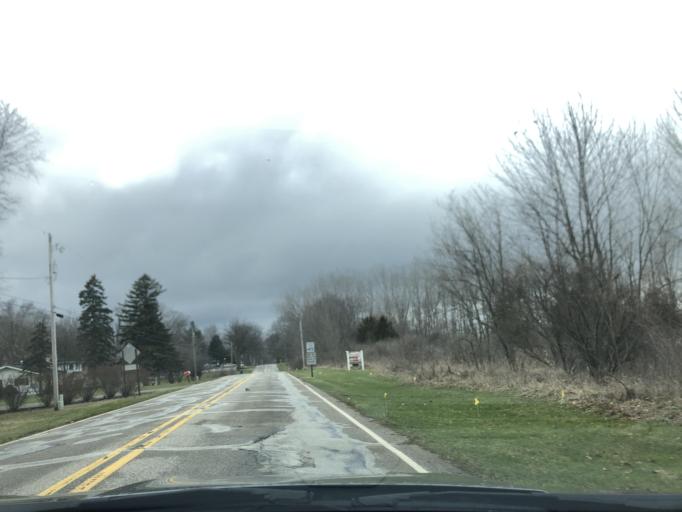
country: US
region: Michigan
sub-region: Clinton County
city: Fowler
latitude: 43.1047
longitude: -84.6810
